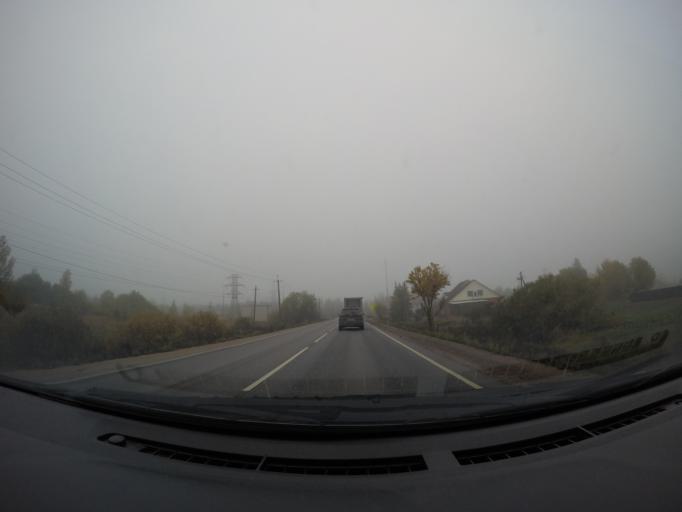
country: RU
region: Moskovskaya
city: Rumyantsevo
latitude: 55.8779
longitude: 36.5678
